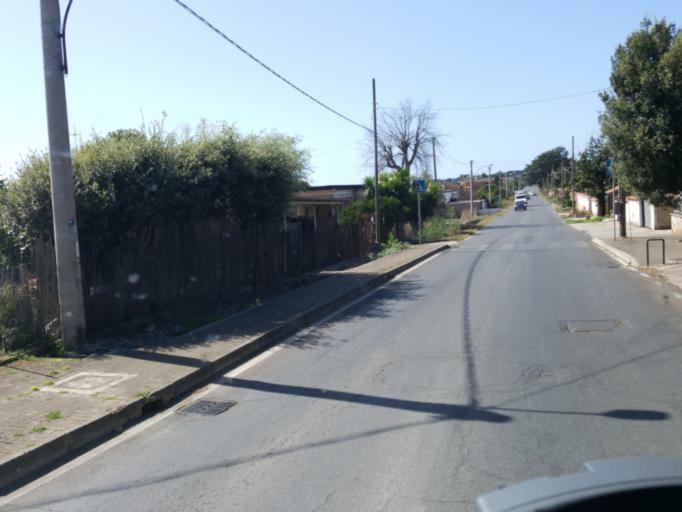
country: IT
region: Latium
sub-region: Citta metropolitana di Roma Capitale
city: Nettuno
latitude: 41.5013
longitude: 12.6851
